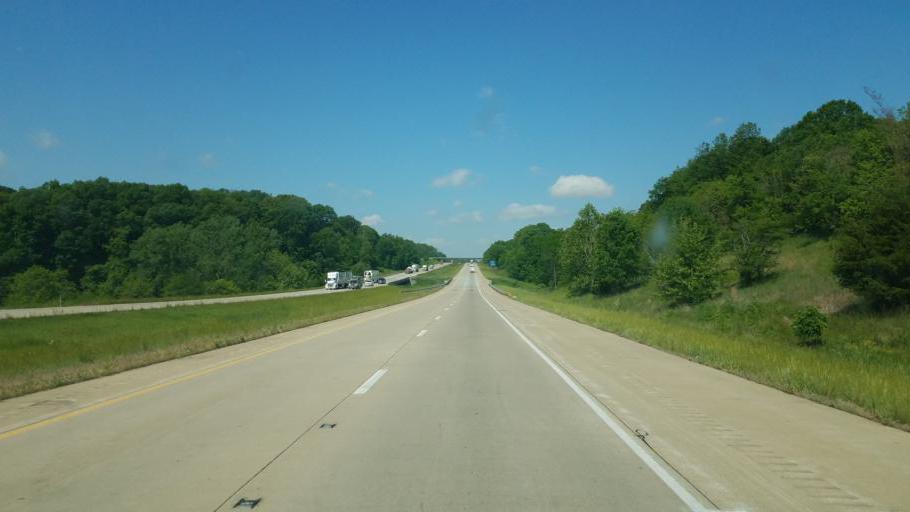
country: US
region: Illinois
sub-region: Clark County
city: Marshall
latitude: 39.4219
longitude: -87.6430
